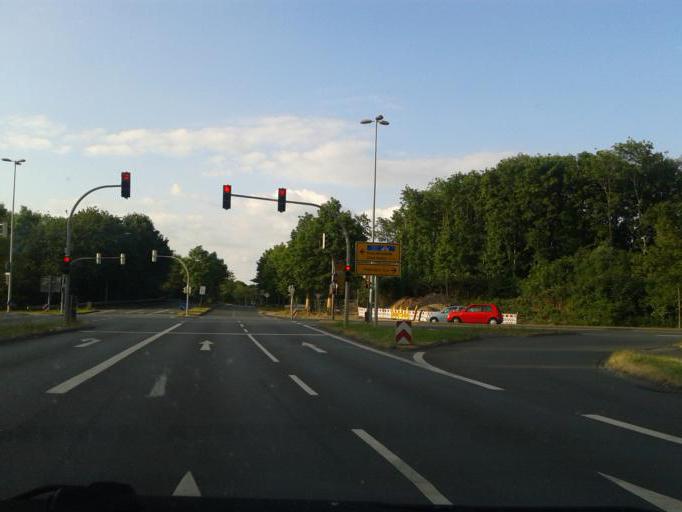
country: DE
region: North Rhine-Westphalia
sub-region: Regierungsbezirk Detmold
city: Paderborn
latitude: 51.7330
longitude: 8.7252
